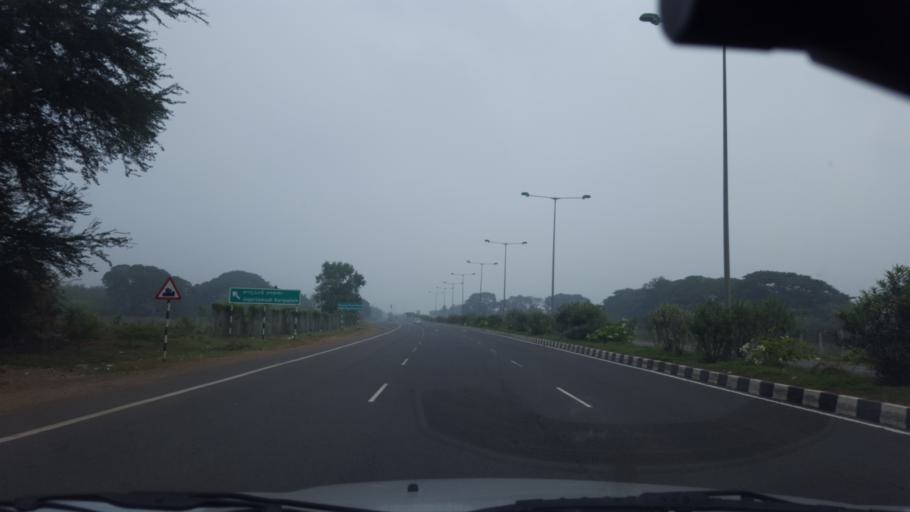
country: IN
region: Andhra Pradesh
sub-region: Prakasam
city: Addanki
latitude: 15.8170
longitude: 80.0430
